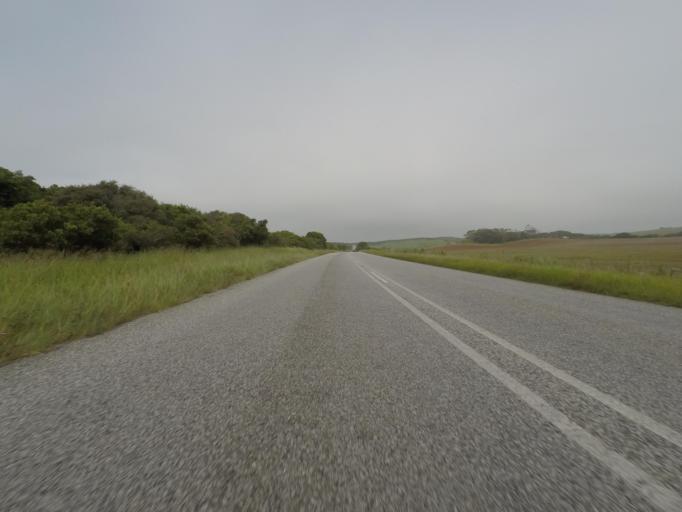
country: ZA
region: Eastern Cape
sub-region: Cacadu District Municipality
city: Port Alfred
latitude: -33.6062
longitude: 26.8269
